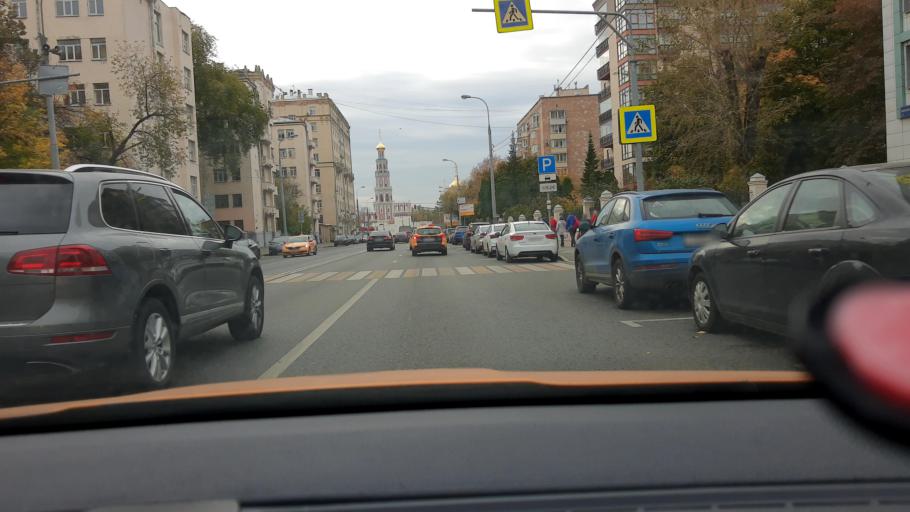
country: RU
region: Moscow
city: Luzhniki
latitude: 55.7281
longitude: 37.5630
